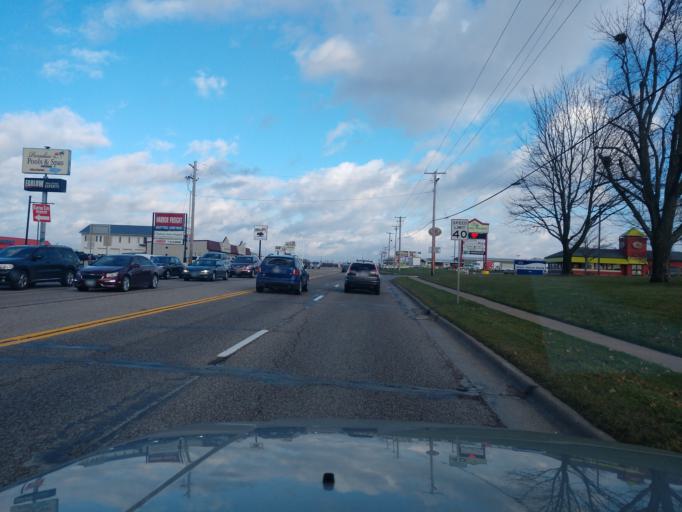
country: US
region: Illinois
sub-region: Adams County
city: Quincy
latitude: 39.9350
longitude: -91.3388
